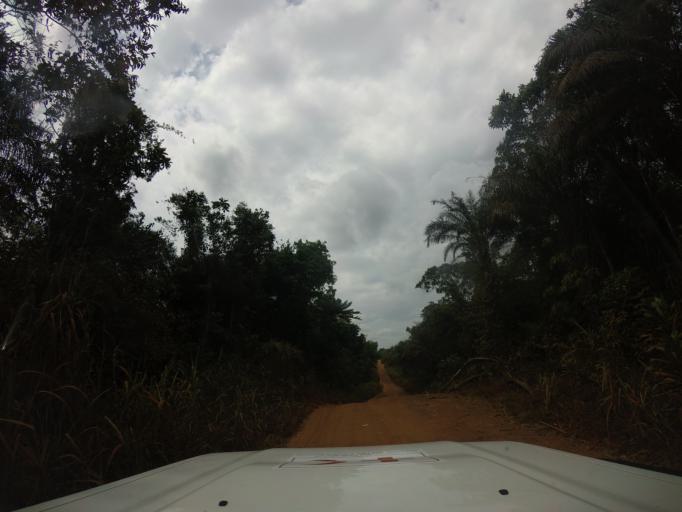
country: LR
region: Grand Cape Mount
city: Robertsport
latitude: 6.9591
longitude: -11.3187
